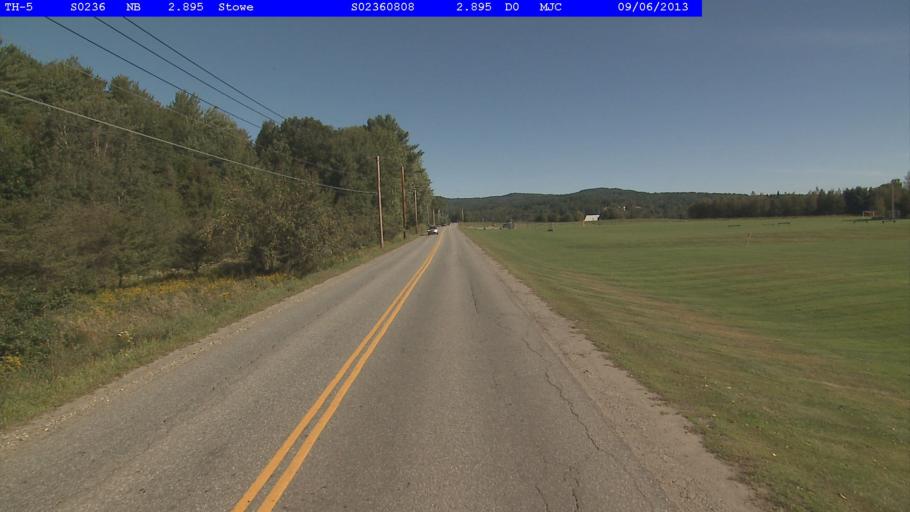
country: US
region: Vermont
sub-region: Washington County
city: Waterbury
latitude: 44.4664
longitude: -72.7281
